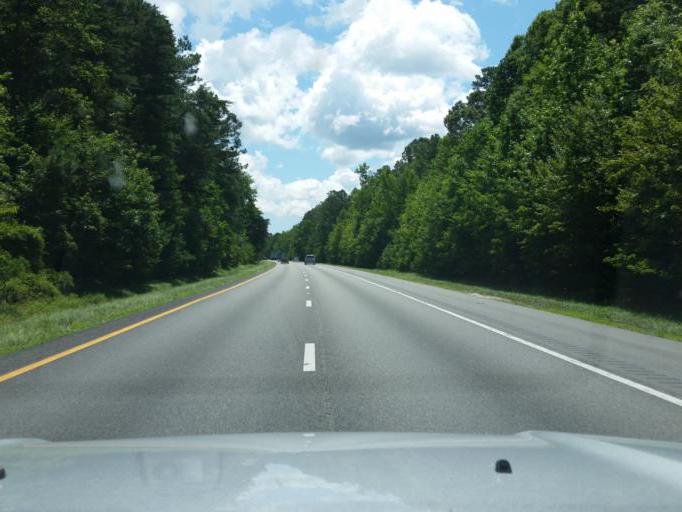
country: US
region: Virginia
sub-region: King William County
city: West Point
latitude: 37.4256
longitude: -76.8357
